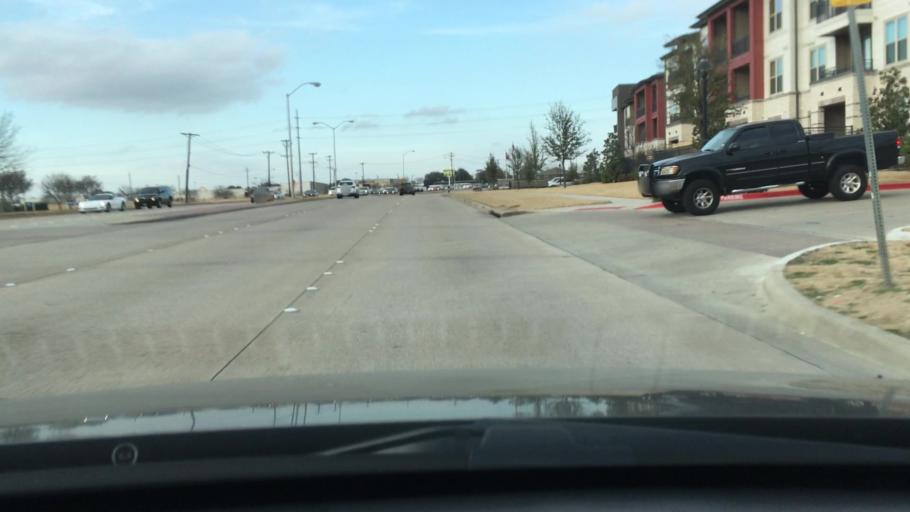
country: US
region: Texas
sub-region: Dallas County
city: Richardson
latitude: 33.0047
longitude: -96.7676
